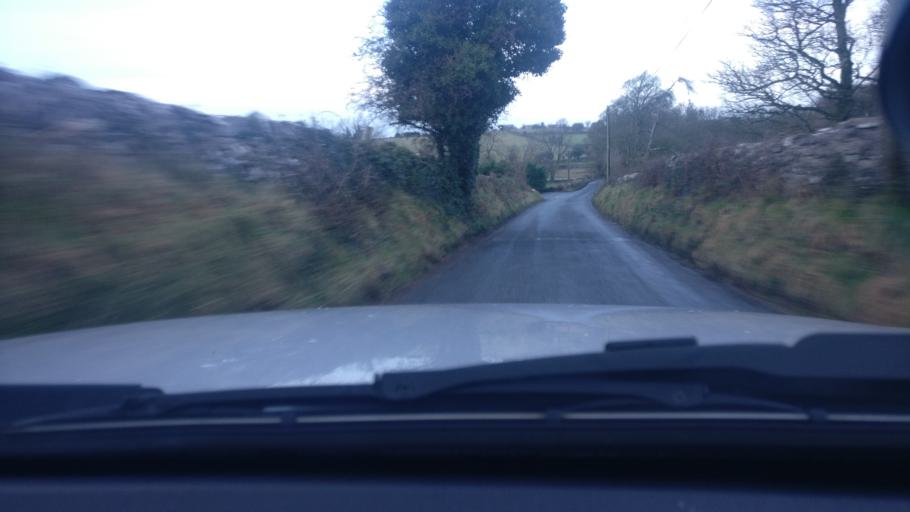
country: IE
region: Connaught
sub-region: County Galway
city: Loughrea
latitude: 53.1870
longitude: -8.6019
